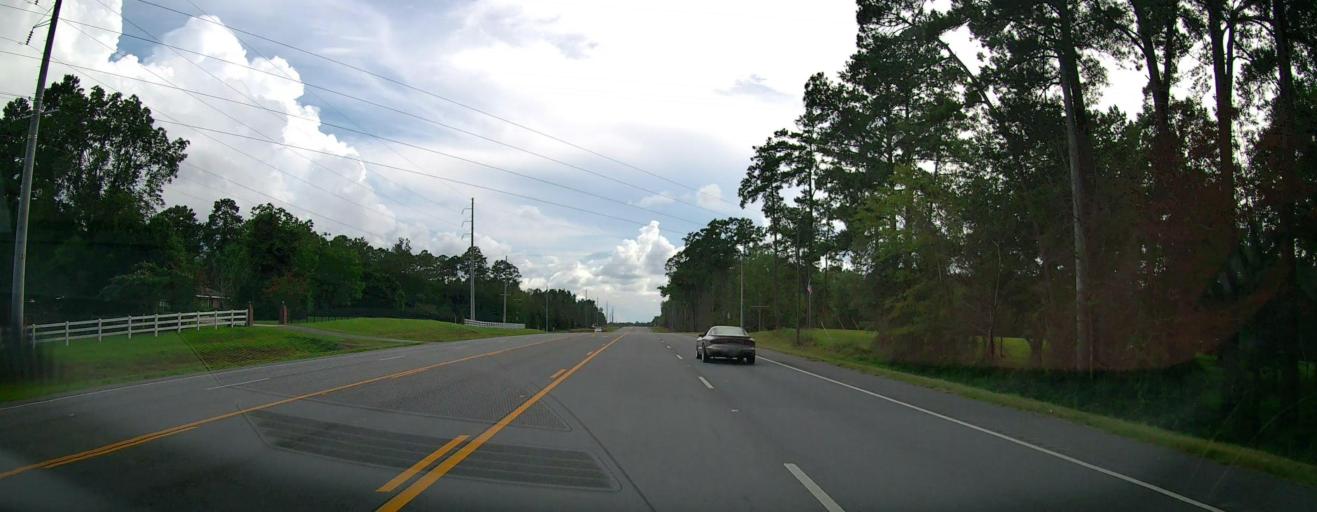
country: US
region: Georgia
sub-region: Wayne County
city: Jesup
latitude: 31.4738
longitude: -82.0347
